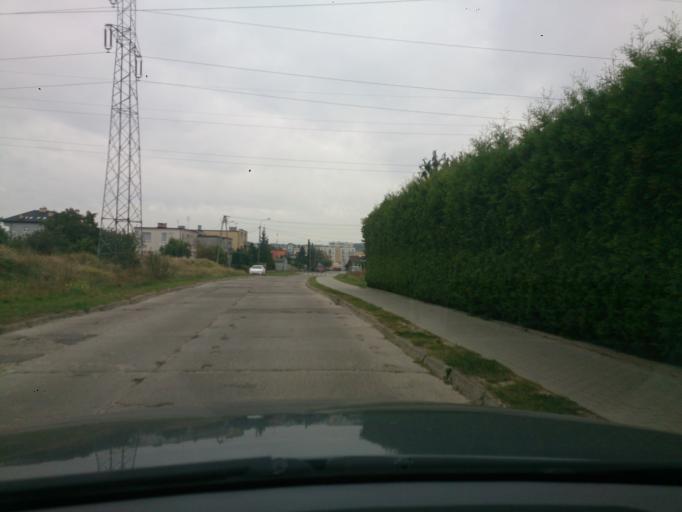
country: PL
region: Pomeranian Voivodeship
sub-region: Powiat wejherowski
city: Reda
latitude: 54.6006
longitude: 18.3611
